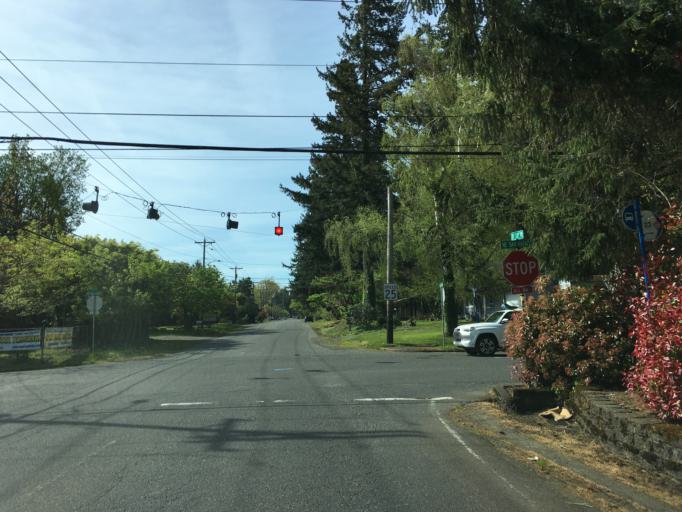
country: US
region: Oregon
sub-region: Multnomah County
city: Lents
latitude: 45.5374
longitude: -122.5272
